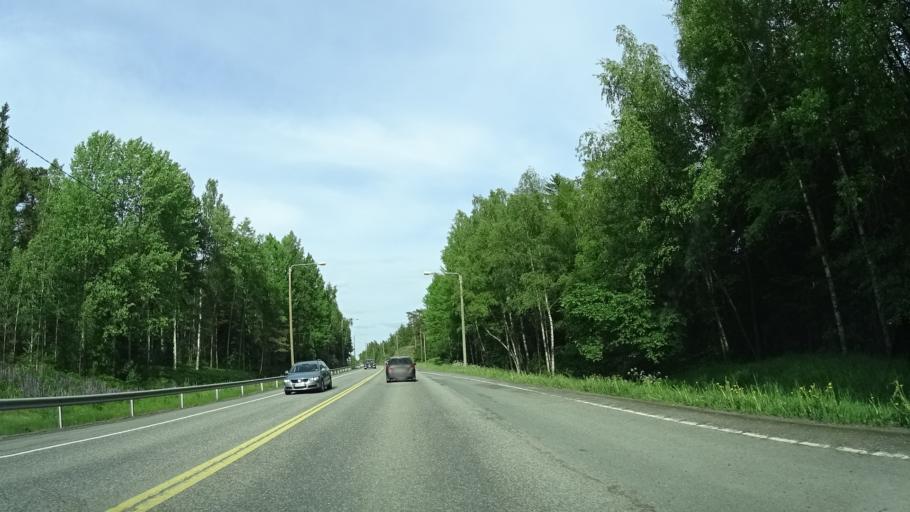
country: FI
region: Uusimaa
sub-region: Helsinki
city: Espoo
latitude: 60.2038
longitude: 24.6090
